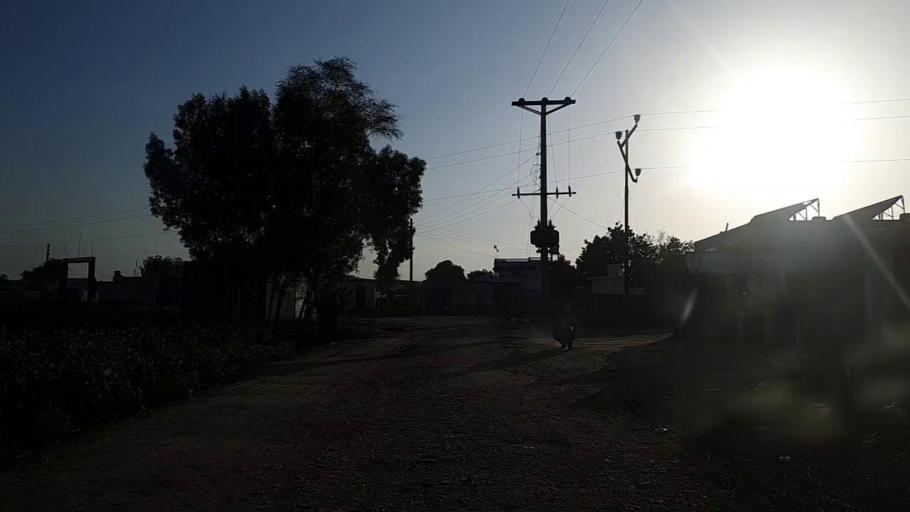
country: PK
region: Sindh
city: Hingorja
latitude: 27.0571
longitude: 68.4039
